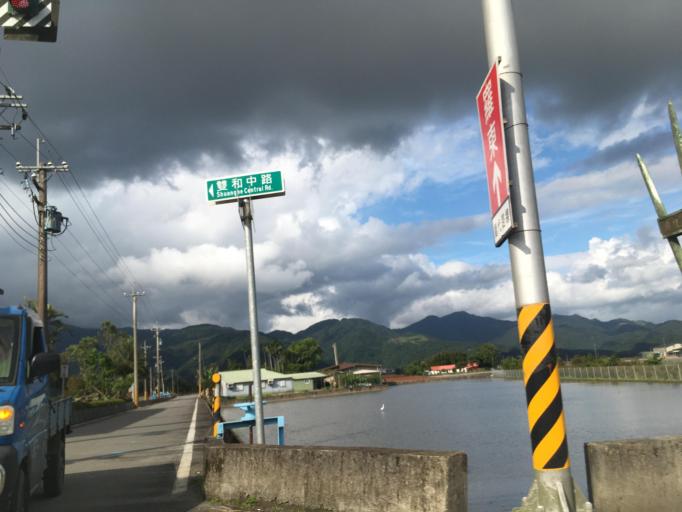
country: TW
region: Taiwan
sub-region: Yilan
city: Yilan
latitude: 24.6675
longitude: 121.6319
